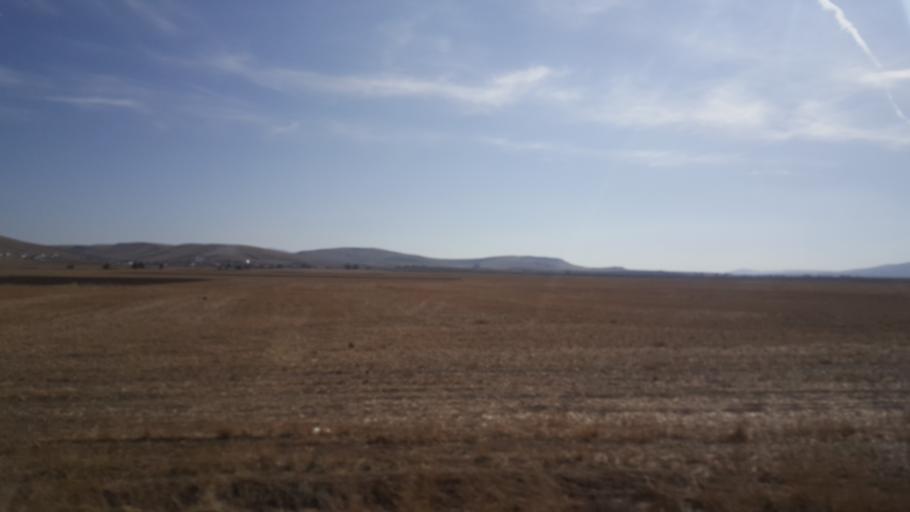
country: TR
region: Ankara
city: Yenice
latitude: 39.3821
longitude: 32.8038
